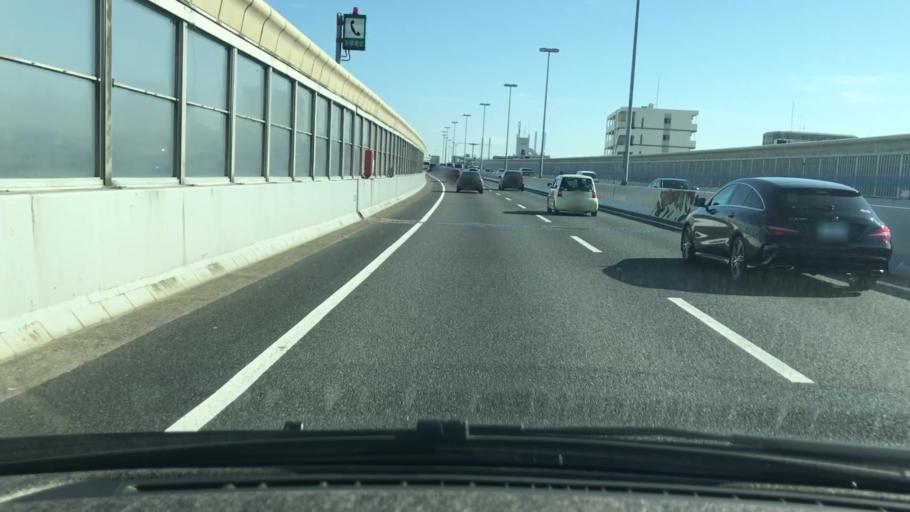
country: JP
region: Hyogo
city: Ashiya
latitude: 34.7112
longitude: 135.2622
